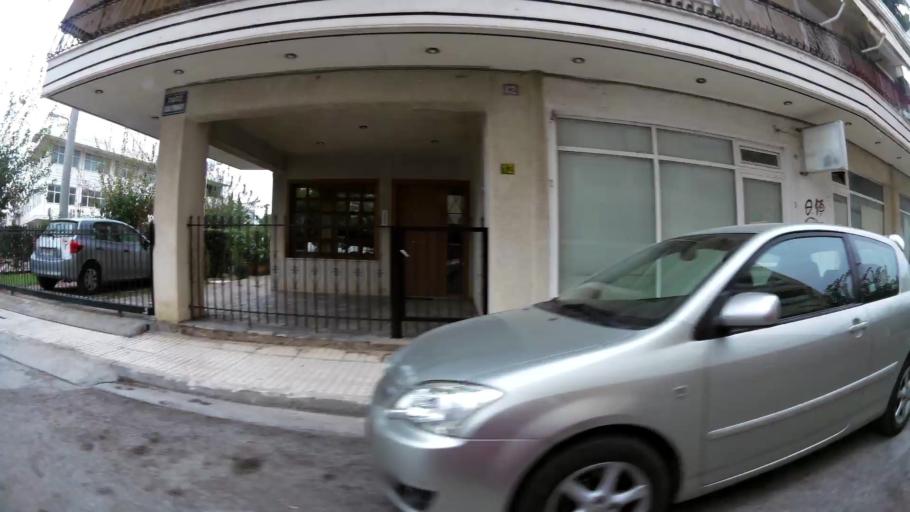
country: GR
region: Attica
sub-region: Nomarchia Athinas
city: Peristeri
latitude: 38.0176
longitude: 23.7052
